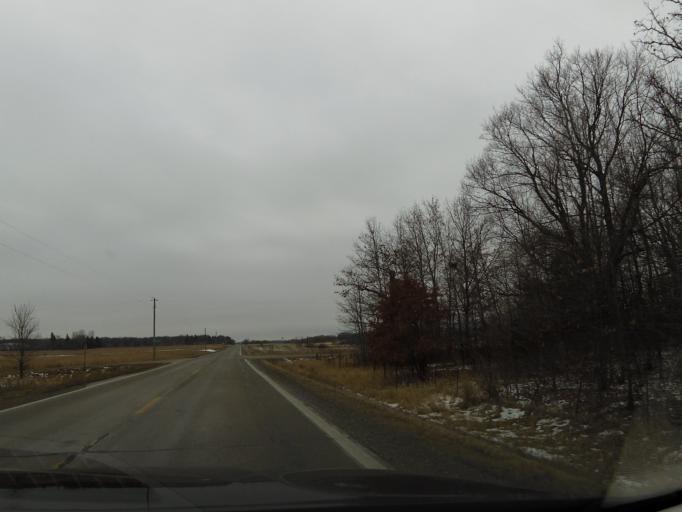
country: US
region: Minnesota
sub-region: Carver County
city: Watertown
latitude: 44.9931
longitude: -93.8488
